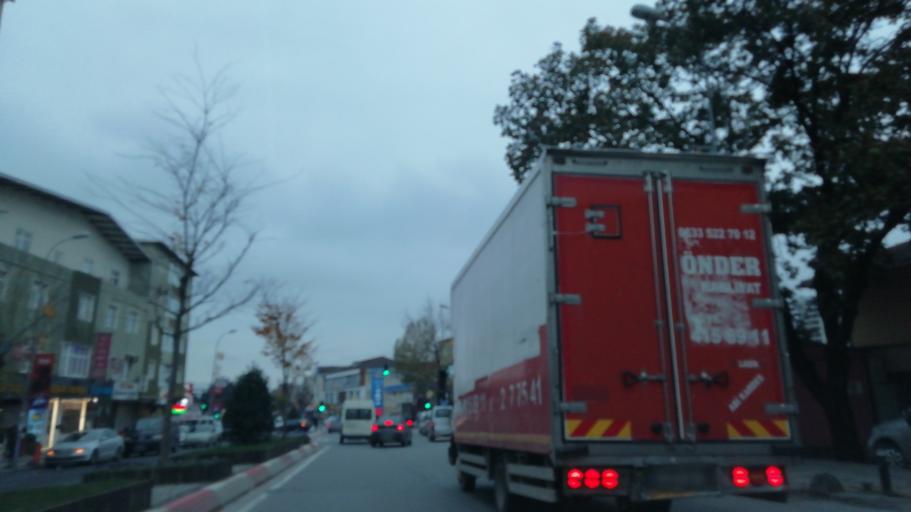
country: TR
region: Istanbul
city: Sultanbeyli
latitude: 40.9710
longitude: 29.2497
